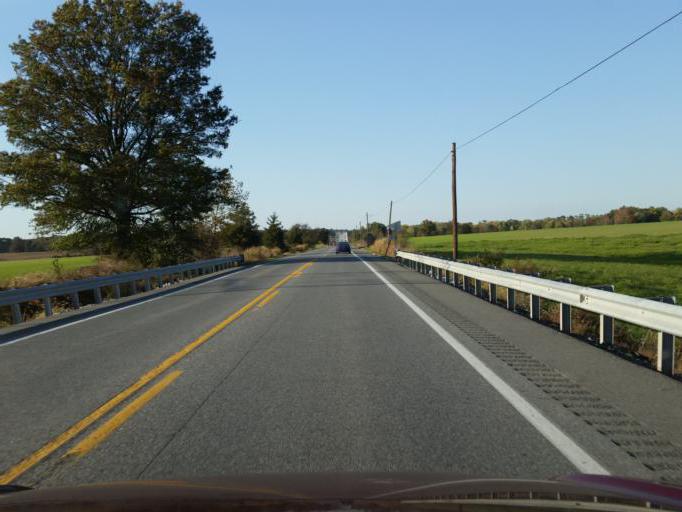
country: US
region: Pennsylvania
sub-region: Lancaster County
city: Elizabethtown
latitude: 40.1916
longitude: -76.6052
